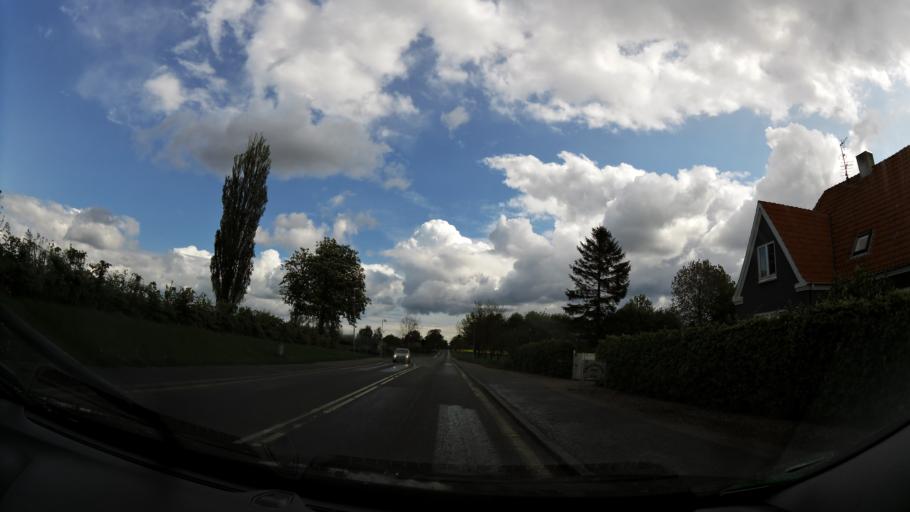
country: DK
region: South Denmark
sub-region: Svendborg Kommune
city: Thuro By
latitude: 55.1096
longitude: 10.7139
